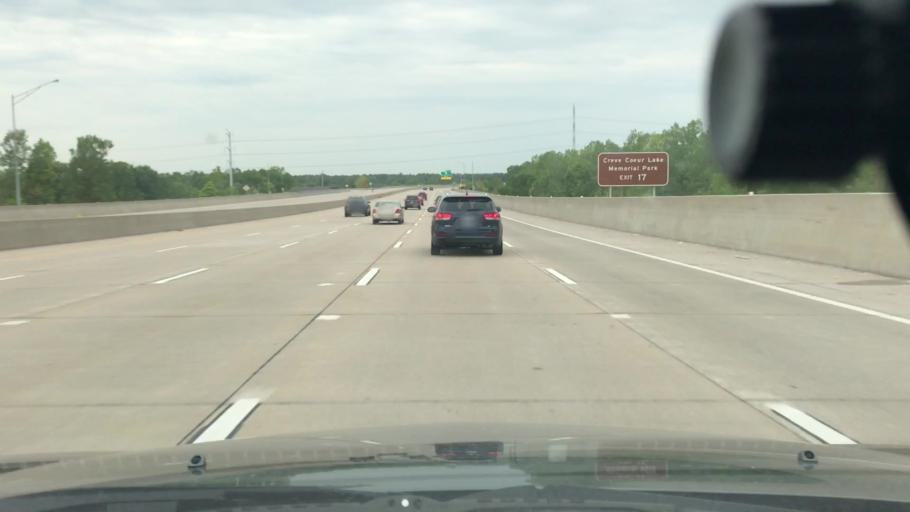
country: US
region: Missouri
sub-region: Saint Louis County
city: Maryland Heights
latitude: 38.7065
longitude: -90.4923
